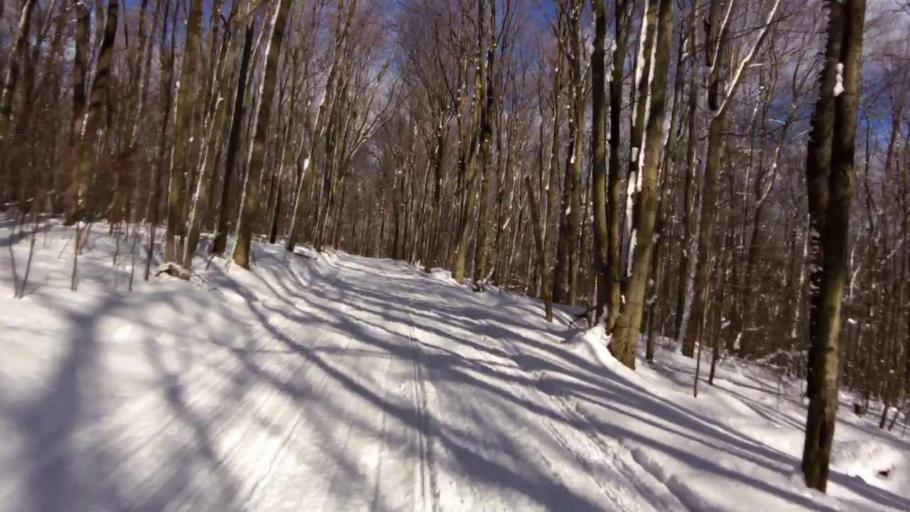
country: US
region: New York
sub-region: Cattaraugus County
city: Salamanca
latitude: 42.0711
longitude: -78.6929
